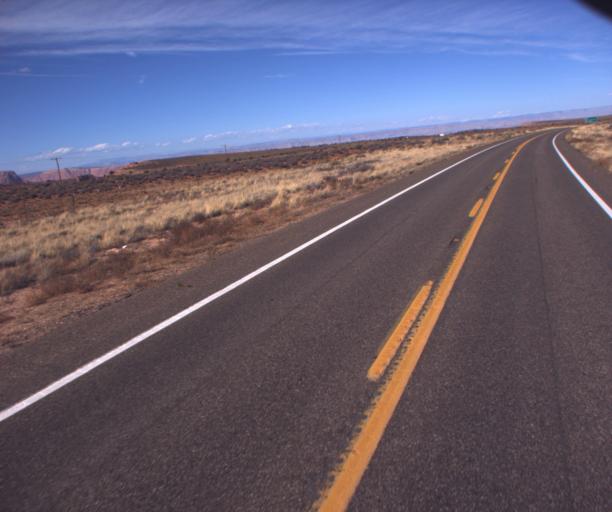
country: US
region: Arizona
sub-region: Coconino County
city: LeChee
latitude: 36.7519
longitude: -111.5740
